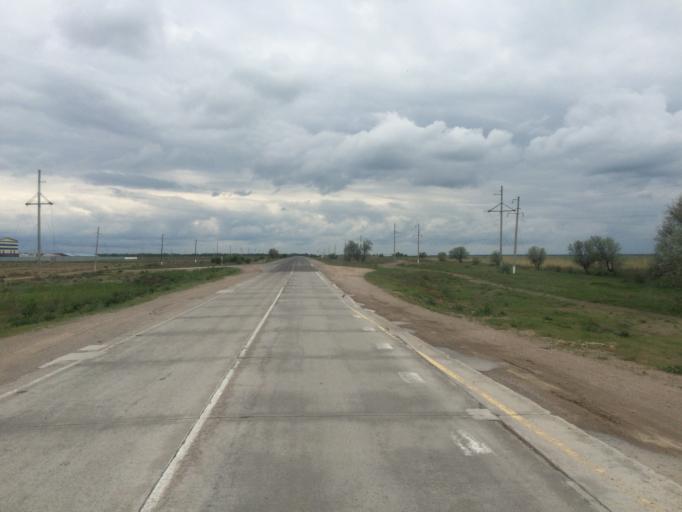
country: KG
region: Chuy
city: Sokuluk
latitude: 43.2696
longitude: 74.2441
